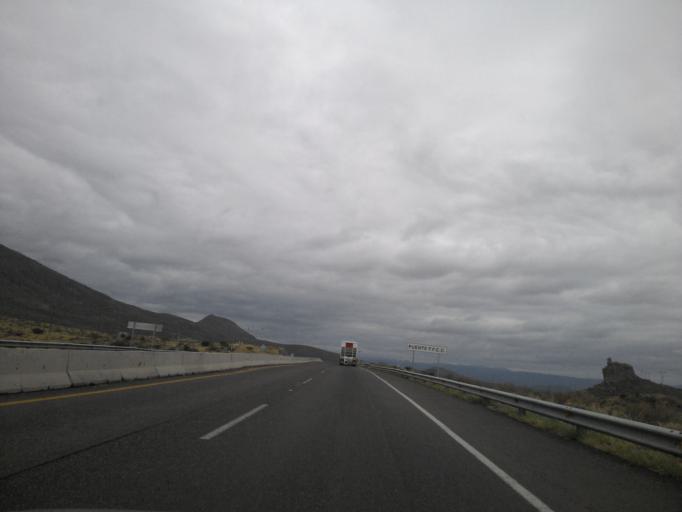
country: MX
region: Durango
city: Cuencame
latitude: 25.1596
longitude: -103.7364
